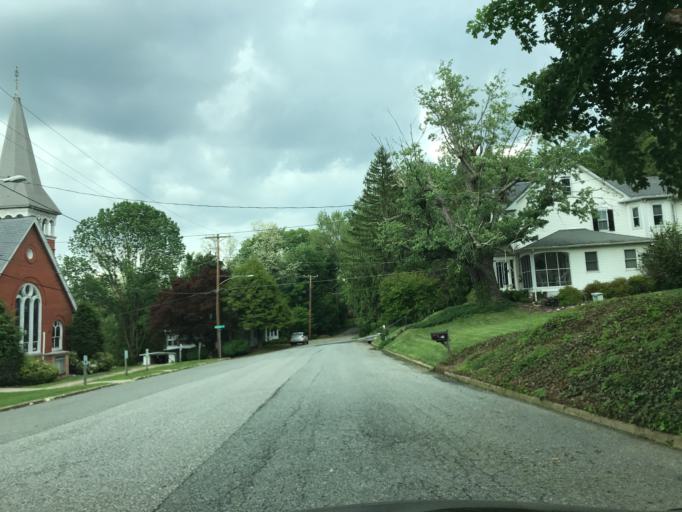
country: US
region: Pennsylvania
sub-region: York County
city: Susquehanna Trails
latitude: 39.7197
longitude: -76.3348
